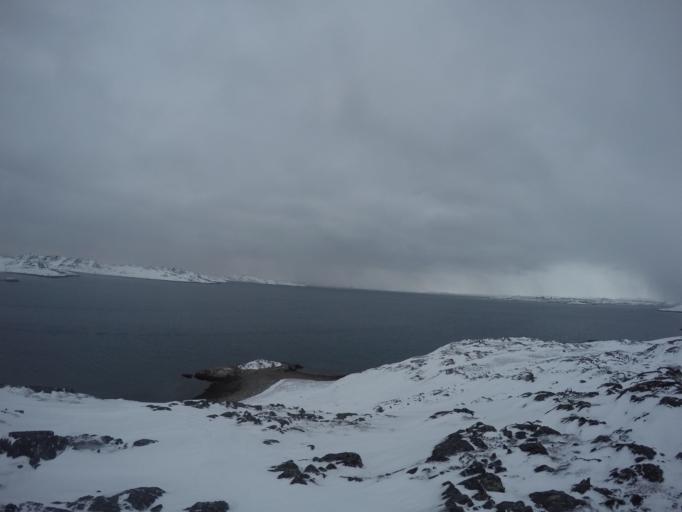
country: GL
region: Sermersooq
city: Nuuk
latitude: 64.1364
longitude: -51.6774
